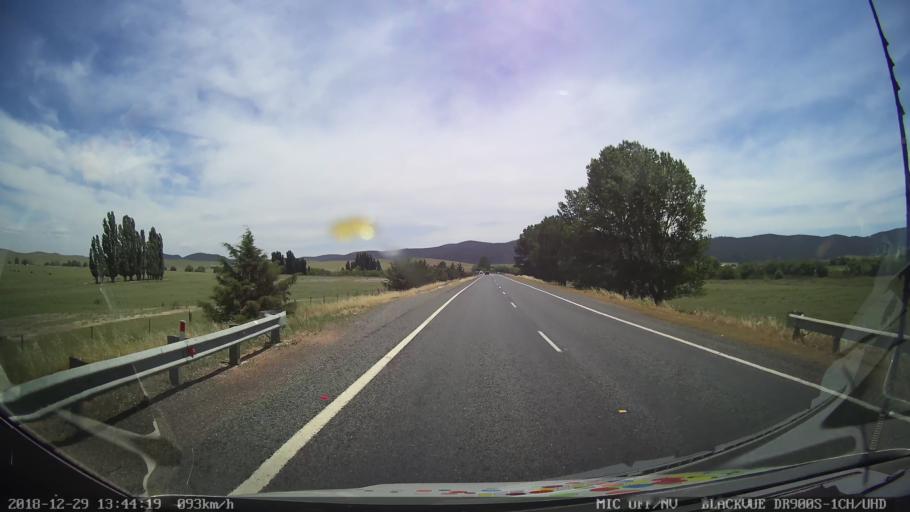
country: AU
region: New South Wales
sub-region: Cooma-Monaro
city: Cooma
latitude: -36.0830
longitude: 149.1541
